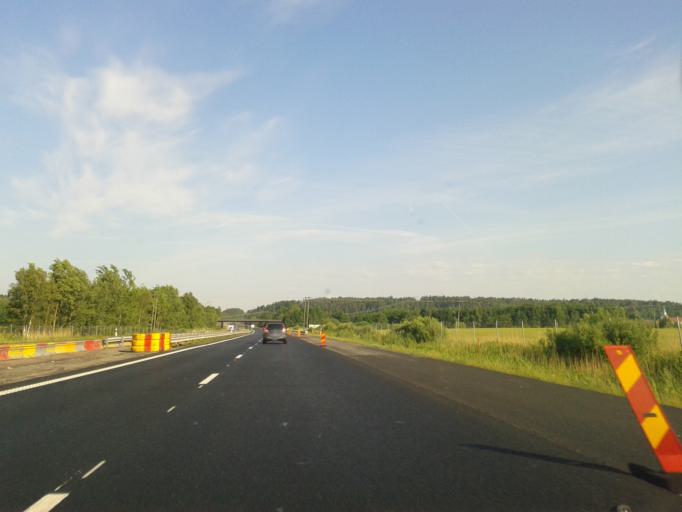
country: SE
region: Vaestra Goetaland
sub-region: Kungalvs Kommun
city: Kungalv
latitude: 57.9011
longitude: 11.9183
